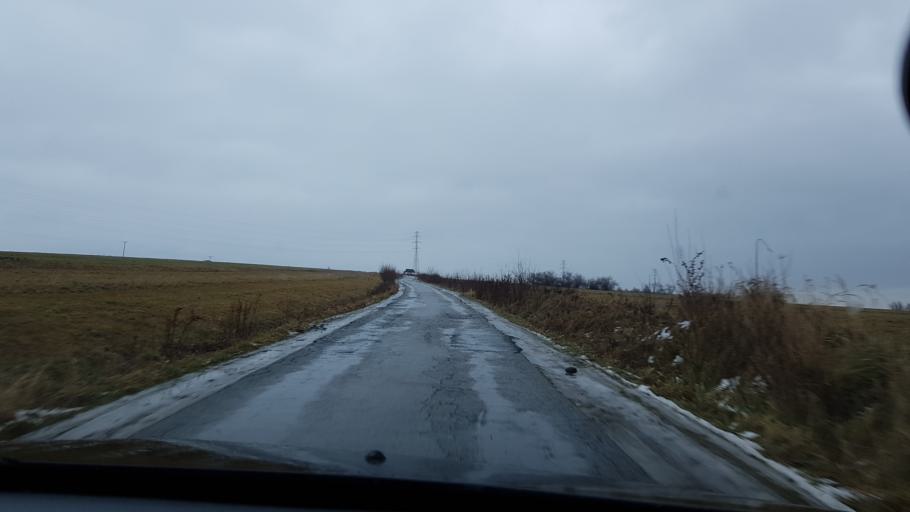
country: PL
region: Lesser Poland Voivodeship
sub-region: Powiat nowotarski
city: Sieniawa
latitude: 49.4881
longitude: 19.9247
